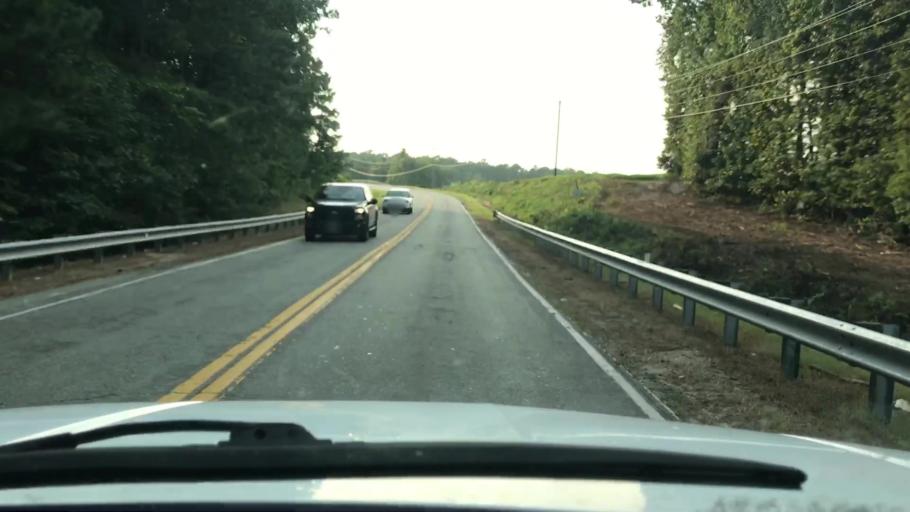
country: US
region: Virginia
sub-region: Chesterfield County
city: Chesterfield
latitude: 37.4111
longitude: -77.5635
